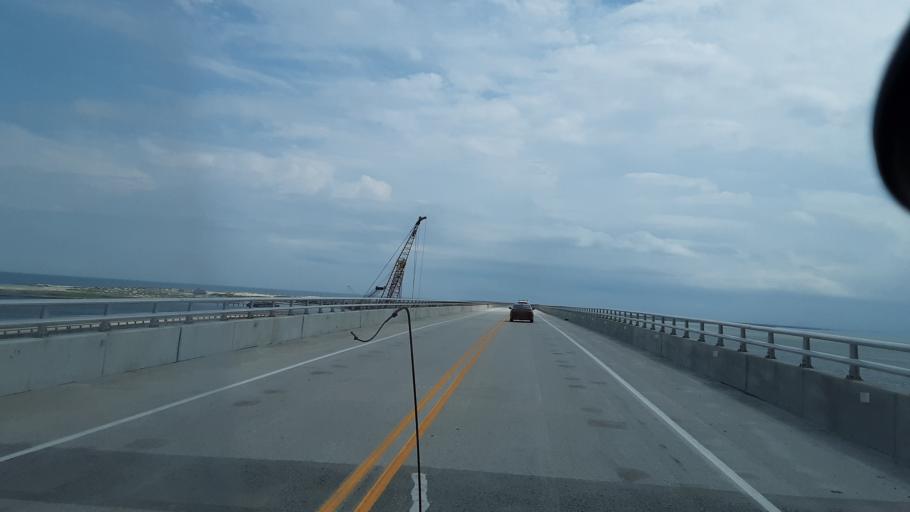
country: US
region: North Carolina
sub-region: Dare County
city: Wanchese
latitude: 35.7731
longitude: -75.5388
